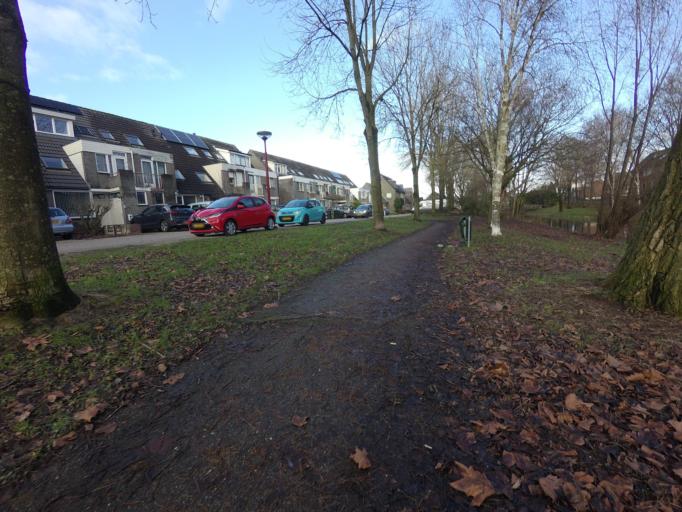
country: NL
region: Utrecht
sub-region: Gemeente Nieuwegein
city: Nieuwegein
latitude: 52.0348
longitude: 5.0697
